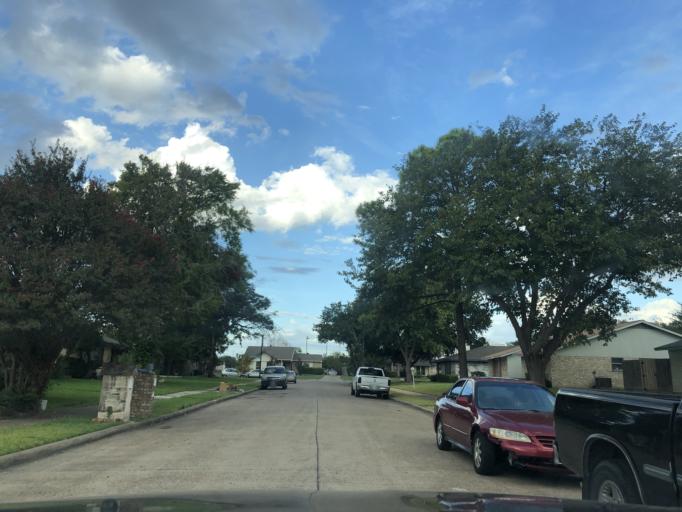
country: US
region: Texas
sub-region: Dallas County
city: Garland
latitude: 32.8728
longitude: -96.6556
